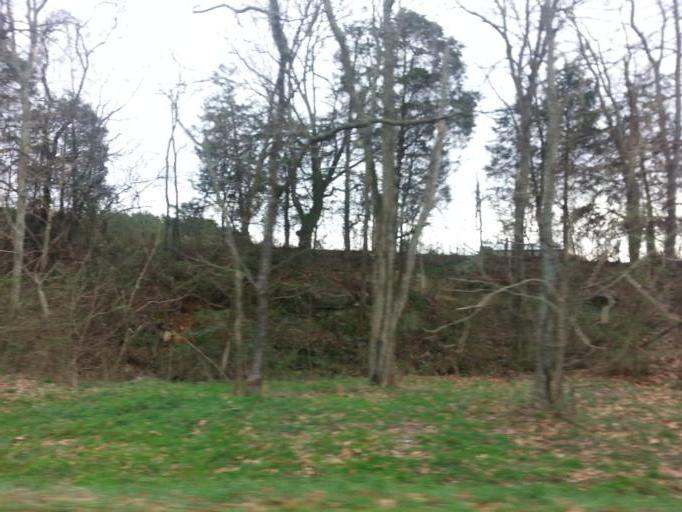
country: US
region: Tennessee
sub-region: Greene County
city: Greeneville
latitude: 36.1182
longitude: -82.9051
